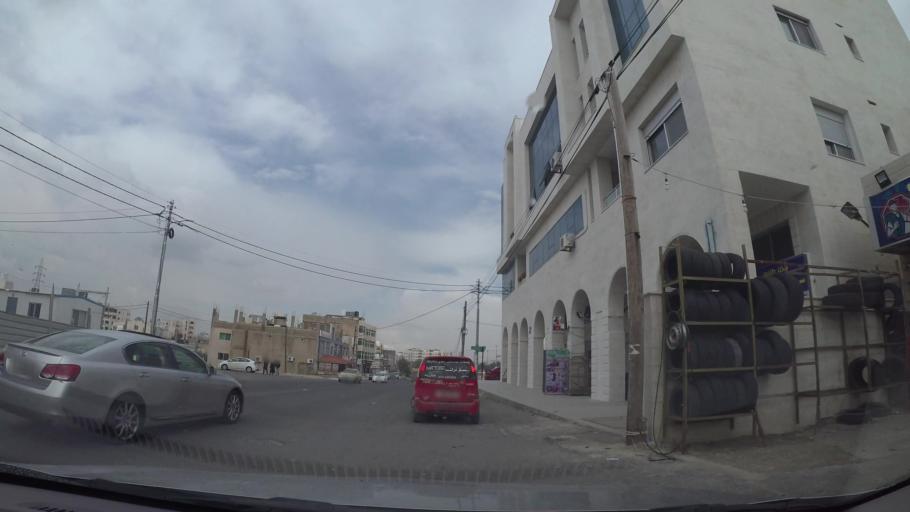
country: JO
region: Amman
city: Umm as Summaq
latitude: 31.8962
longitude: 35.8646
